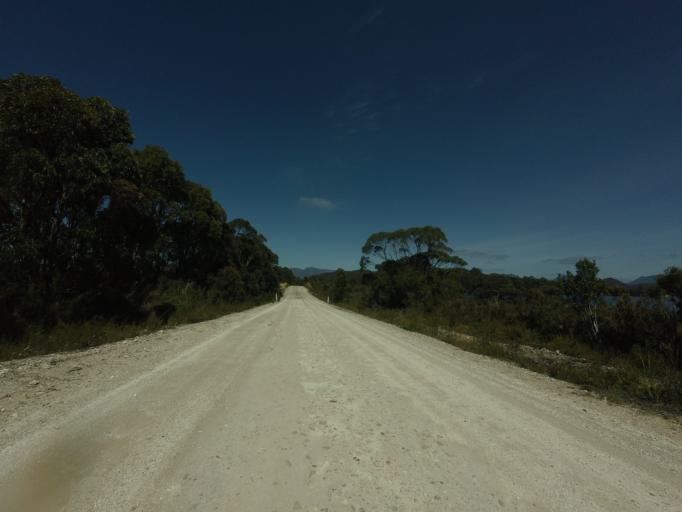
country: AU
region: Tasmania
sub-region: Huon Valley
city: Geeveston
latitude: -43.0270
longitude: 146.3531
